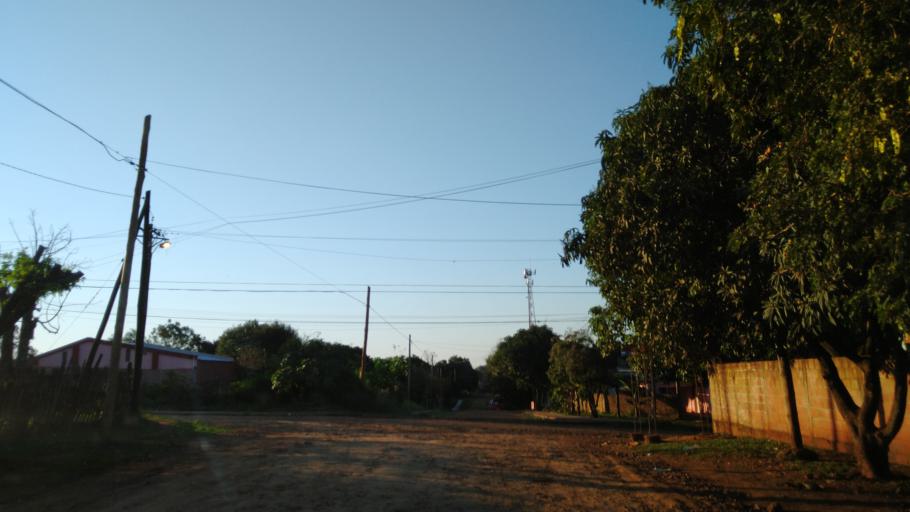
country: AR
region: Misiones
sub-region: Departamento de Capital
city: Posadas
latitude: -27.4187
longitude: -55.9201
